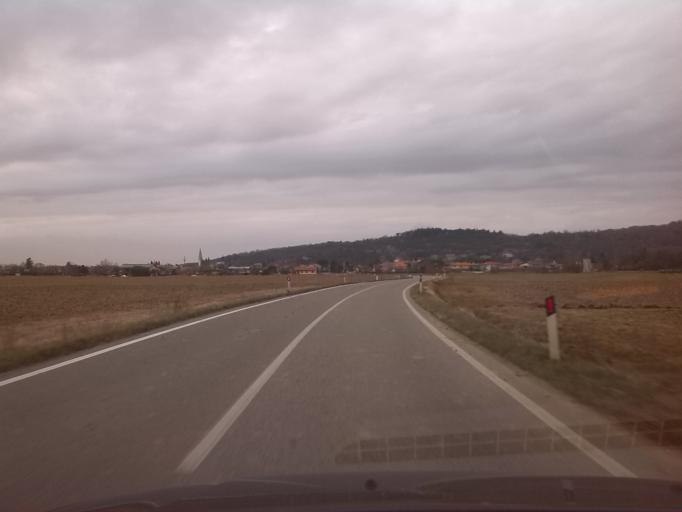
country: IT
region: Friuli Venezia Giulia
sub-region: Provincia di Gorizia
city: Medea
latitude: 45.9115
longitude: 13.4326
